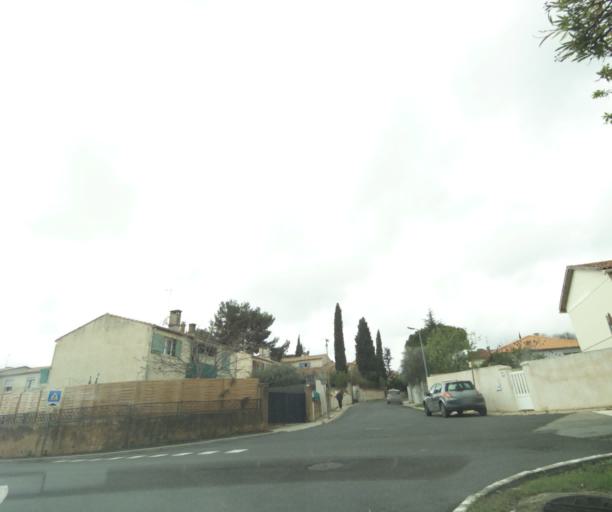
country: FR
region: Languedoc-Roussillon
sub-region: Departement de l'Herault
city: Pignan
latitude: 43.5858
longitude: 3.7603
